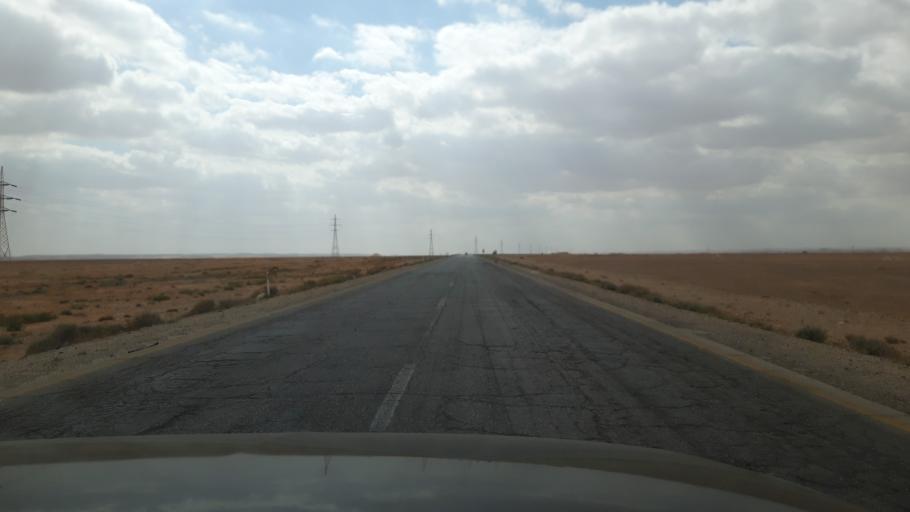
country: JO
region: Amman
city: Sahab
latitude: 31.7615
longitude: 36.3138
